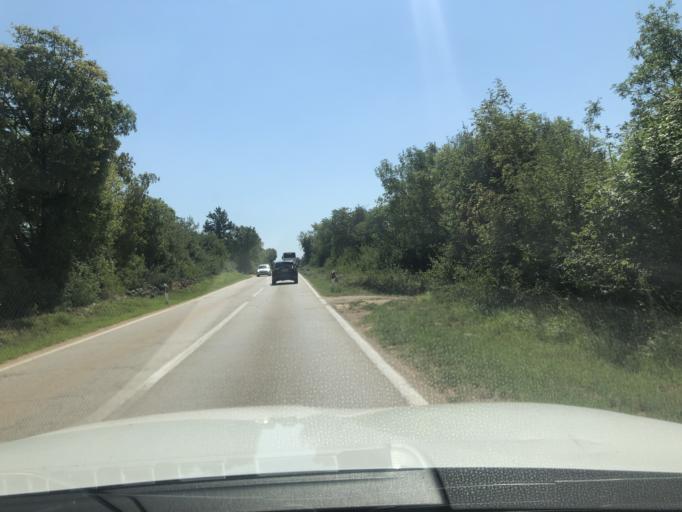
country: HR
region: Istarska
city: Vodnjan
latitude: 45.0276
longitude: 13.7986
